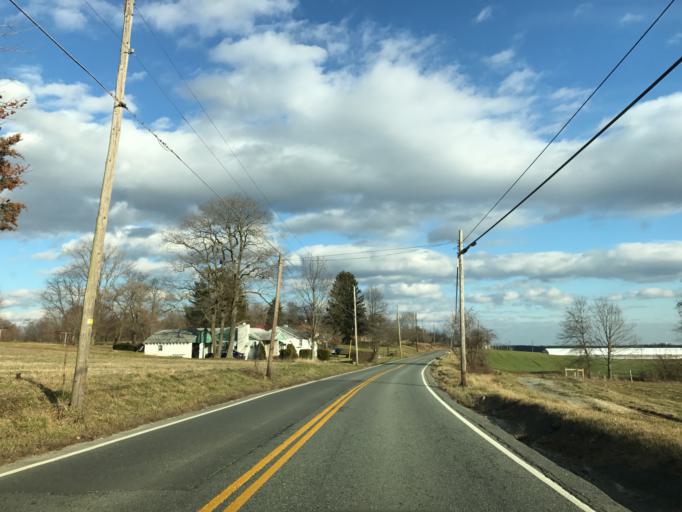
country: US
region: Maryland
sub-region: Cecil County
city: Rising Sun
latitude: 39.6367
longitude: -76.0659
